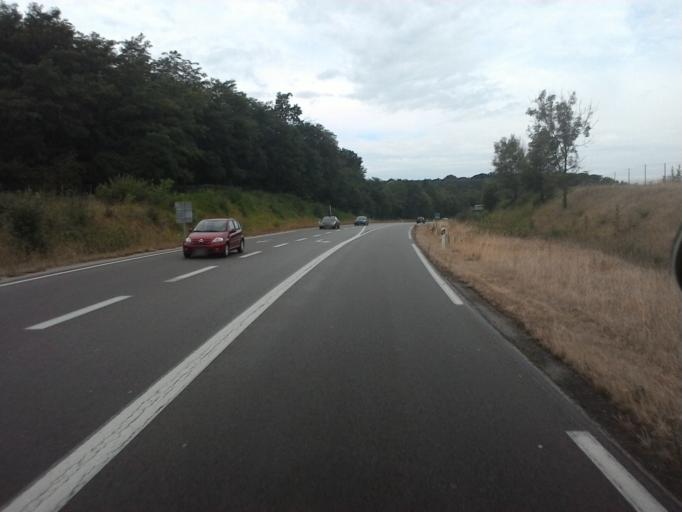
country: FR
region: Franche-Comte
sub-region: Departement du Jura
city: Poligny
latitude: 46.8373
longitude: 5.6819
